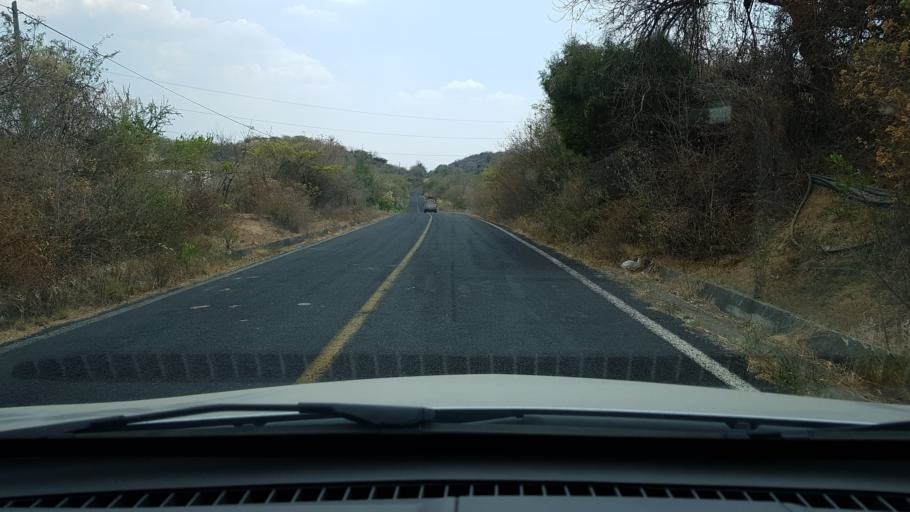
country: MX
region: Morelos
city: Tlacotepec
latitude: 18.8301
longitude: -98.7383
